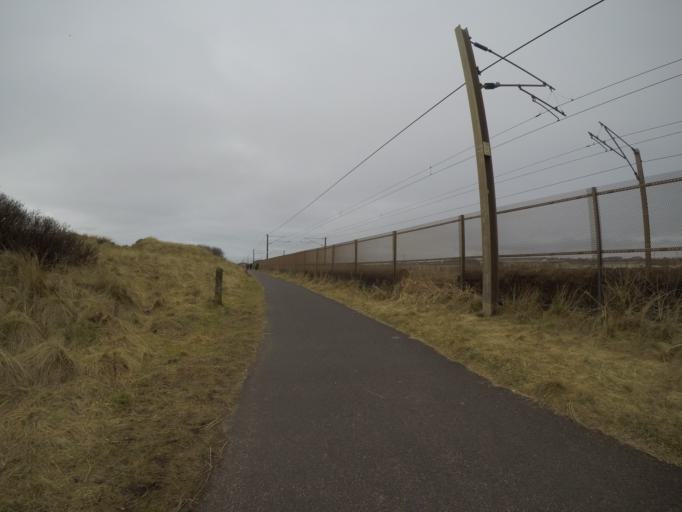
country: GB
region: Scotland
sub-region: North Ayrshire
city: Stevenston
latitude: 55.6324
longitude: -4.7632
